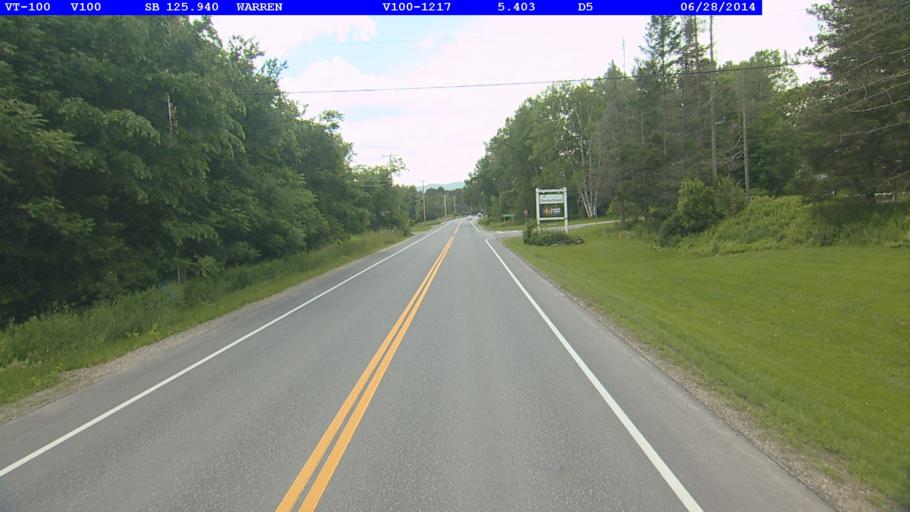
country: US
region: Vermont
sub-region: Washington County
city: Northfield
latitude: 44.1343
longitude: -72.8473
